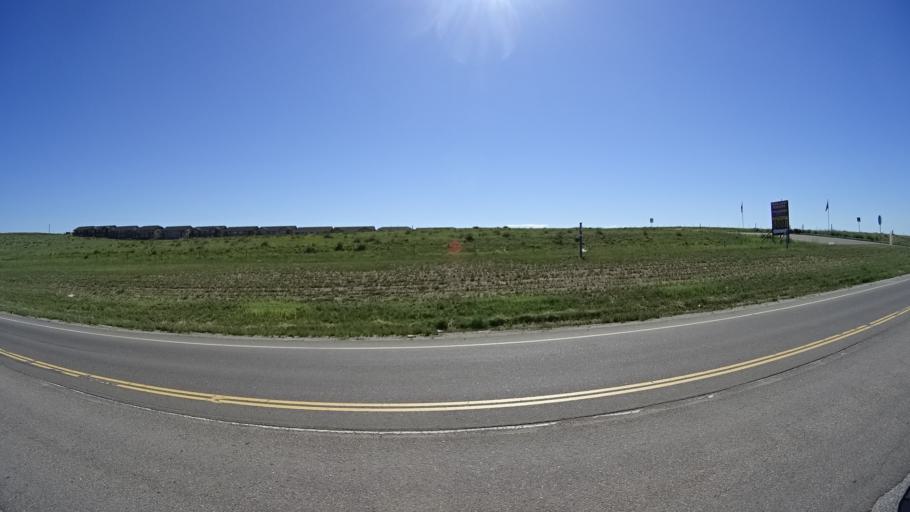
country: US
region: Colorado
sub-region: El Paso County
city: Cimarron Hills
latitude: 38.8943
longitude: -104.6831
